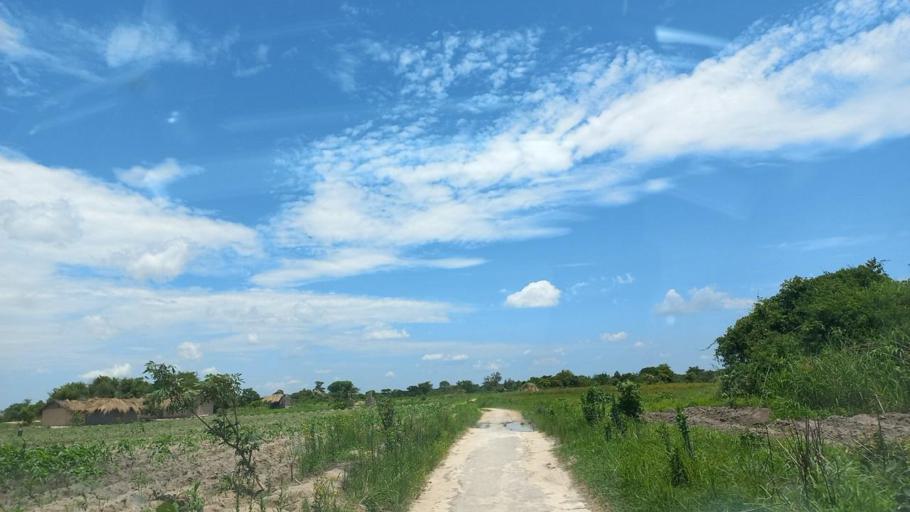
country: ZM
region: Copperbelt
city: Ndola
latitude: -12.8682
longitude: 28.4373
